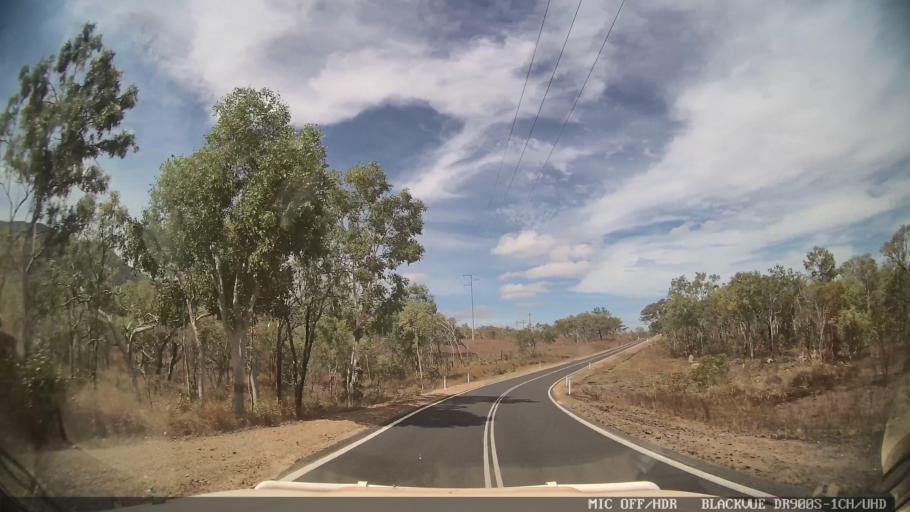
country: AU
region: Queensland
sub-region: Cairns
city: Port Douglas
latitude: -16.6680
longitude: 145.2654
